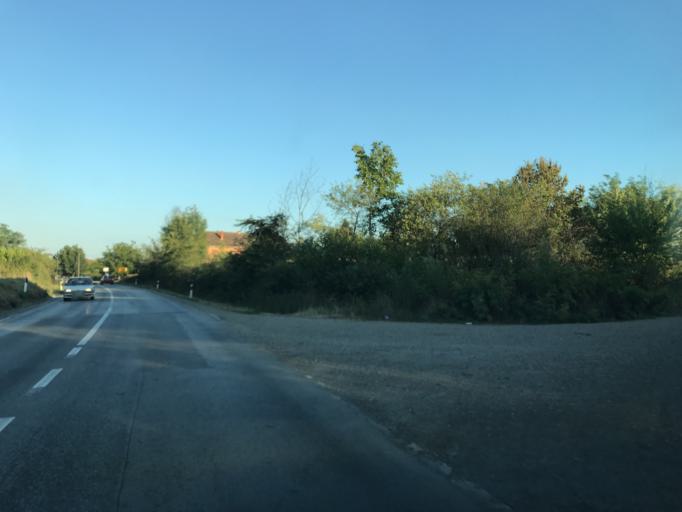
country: RS
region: Central Serbia
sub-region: Podunavski Okrug
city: Smederevo
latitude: 44.5977
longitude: 20.9656
